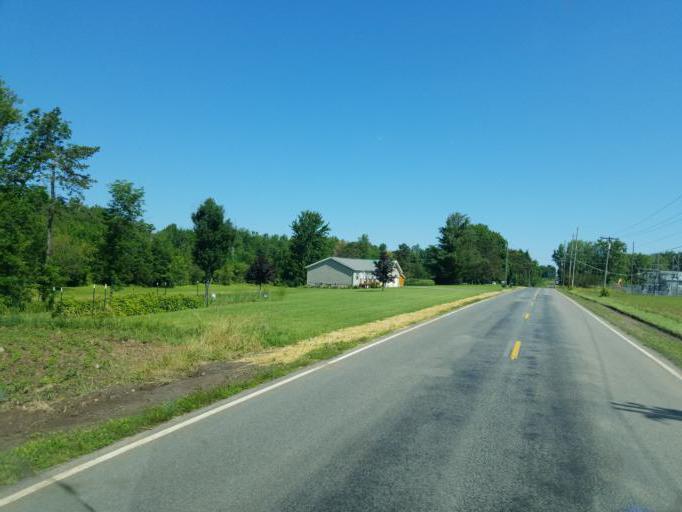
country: US
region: New York
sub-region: Wayne County
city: Wolcott
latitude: 43.2222
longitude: -76.8800
